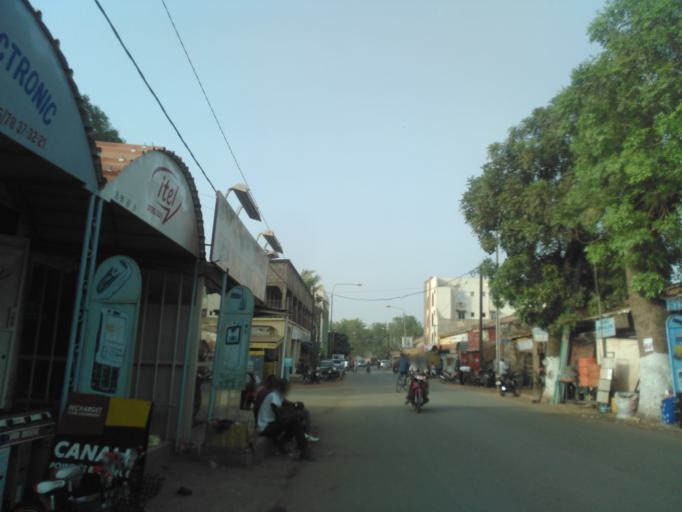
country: BF
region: High-Basins
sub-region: Province du Houet
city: Bobo-Dioulasso
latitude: 11.1734
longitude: -4.2976
